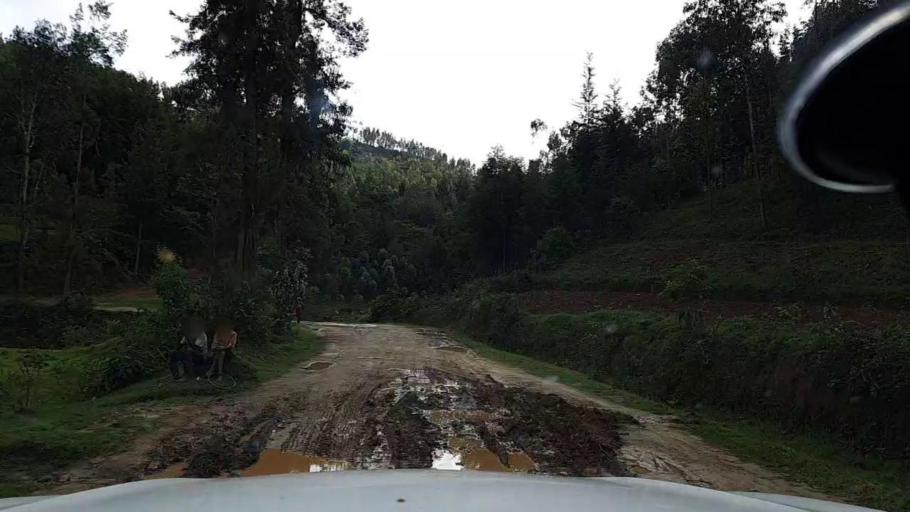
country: RW
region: Western Province
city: Kibuye
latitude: -2.1579
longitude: 29.5450
